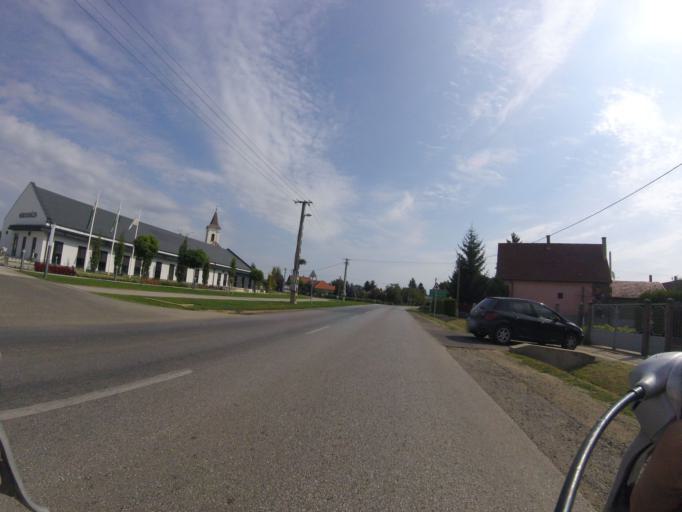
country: HU
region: Szabolcs-Szatmar-Bereg
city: Kemecse
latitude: 48.0685
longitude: 21.8015
